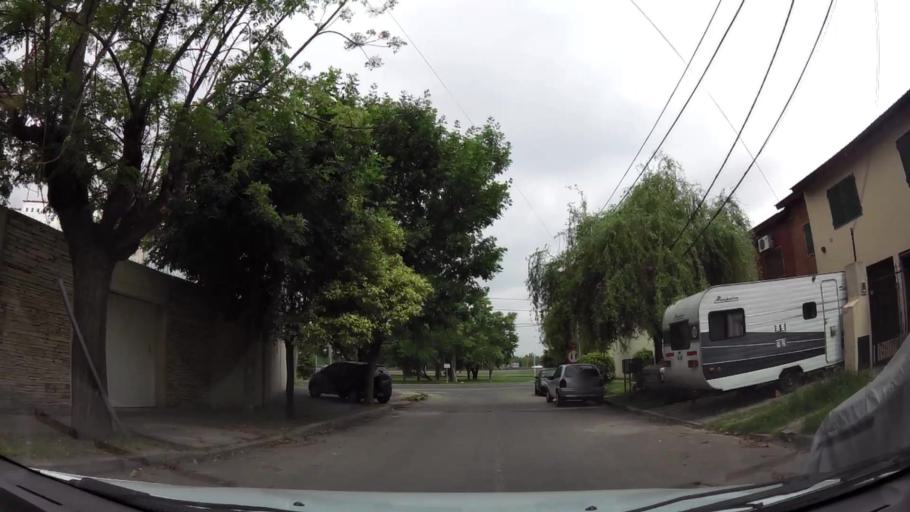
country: AR
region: Buenos Aires
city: San Justo
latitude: -34.7317
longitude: -58.5190
